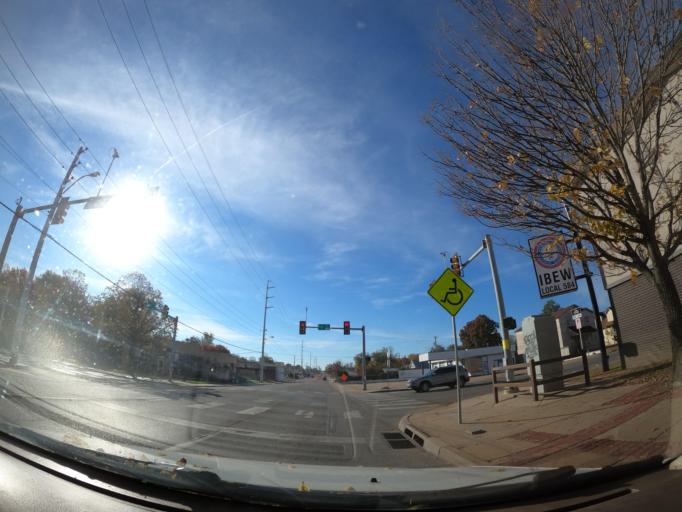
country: US
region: Oklahoma
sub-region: Tulsa County
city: Tulsa
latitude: 36.1519
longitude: -95.9582
